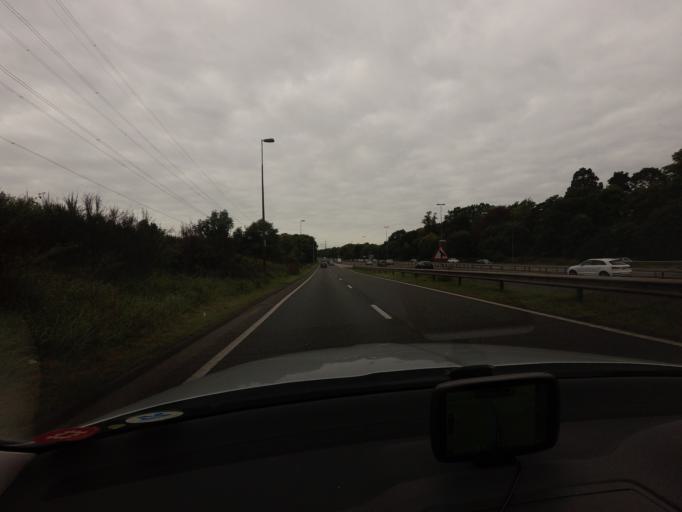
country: GB
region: England
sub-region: Surrey
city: Cobham
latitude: 51.3331
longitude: -0.4314
